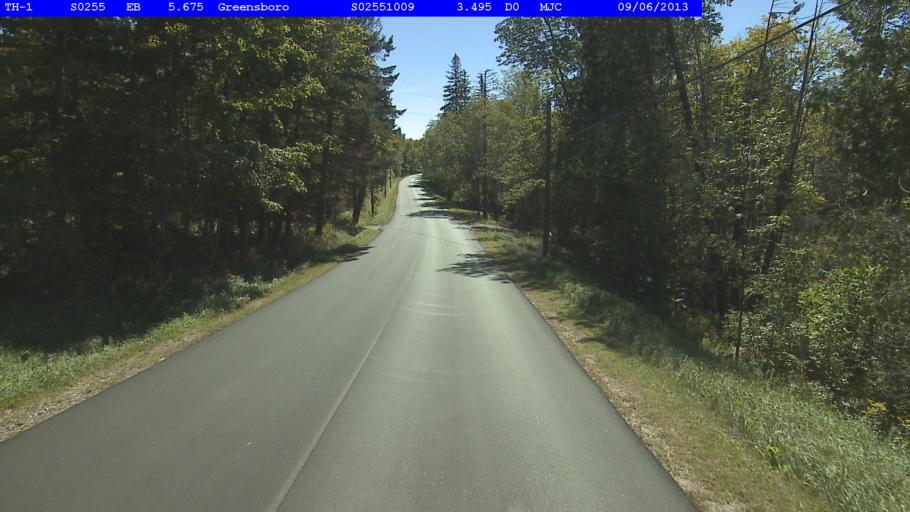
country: US
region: Vermont
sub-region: Caledonia County
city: Hardwick
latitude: 44.5976
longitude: -72.3040
